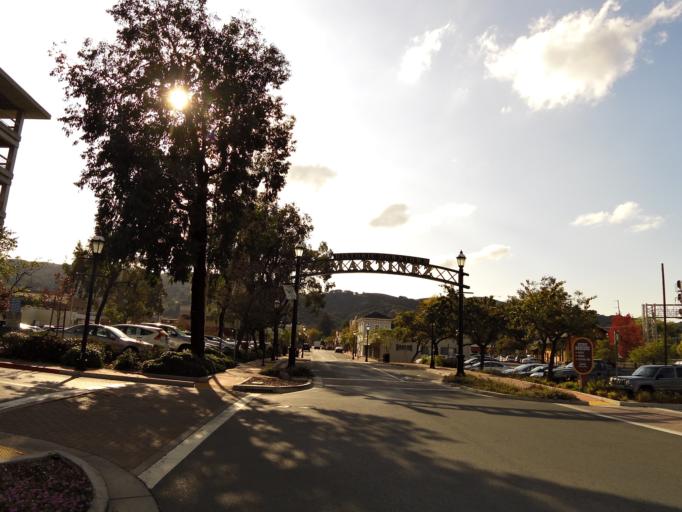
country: US
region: California
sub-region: Contra Costa County
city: Martinez
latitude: 38.0196
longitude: -122.1353
